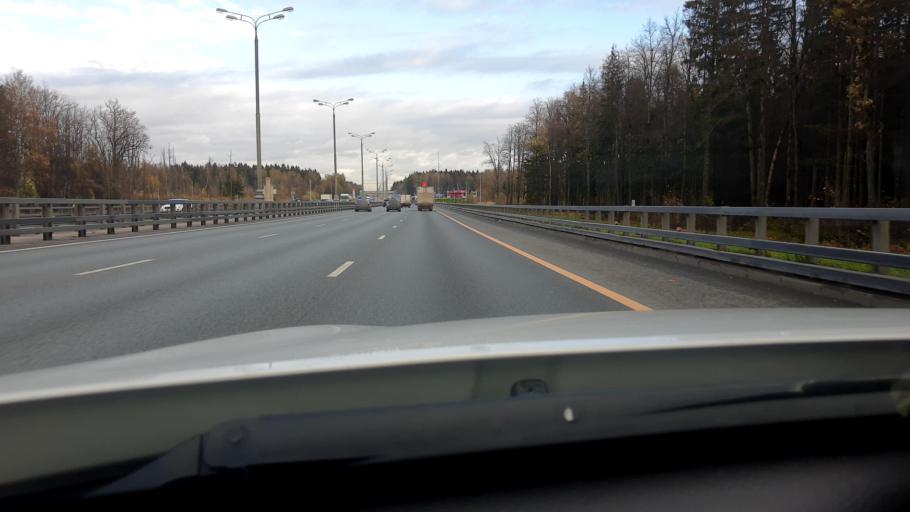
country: RU
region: Moskovskaya
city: Aprelevka
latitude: 55.5483
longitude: 37.1209
